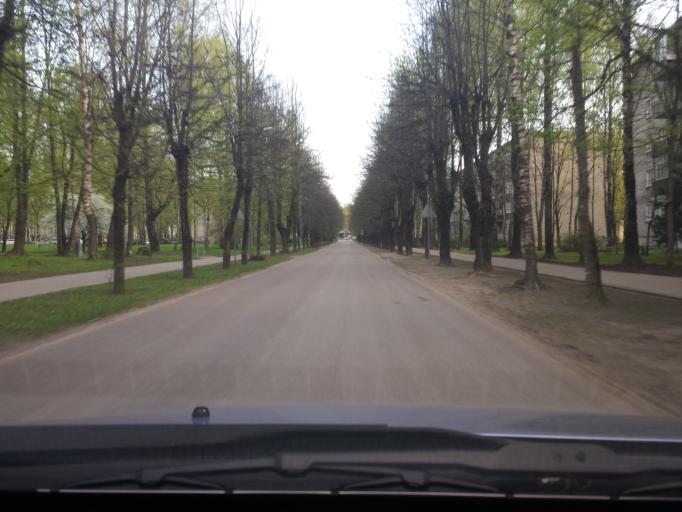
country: LV
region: Riga
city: Bergi
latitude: 56.9927
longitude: 24.2396
